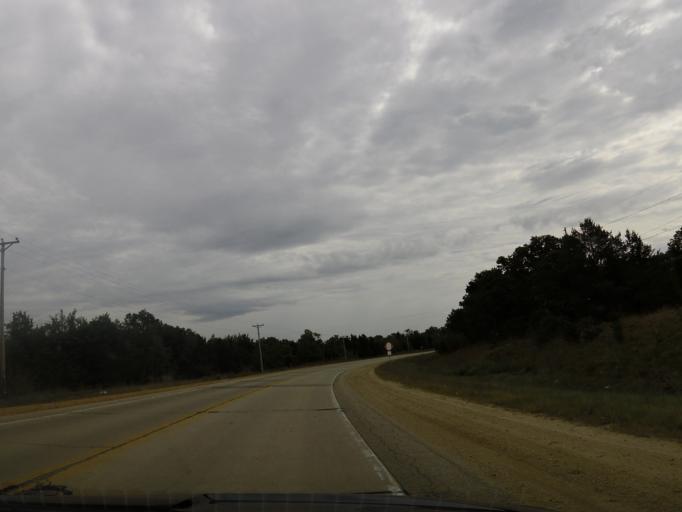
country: US
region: Wisconsin
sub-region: Monroe County
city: Sparta
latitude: 43.9420
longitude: -90.7565
